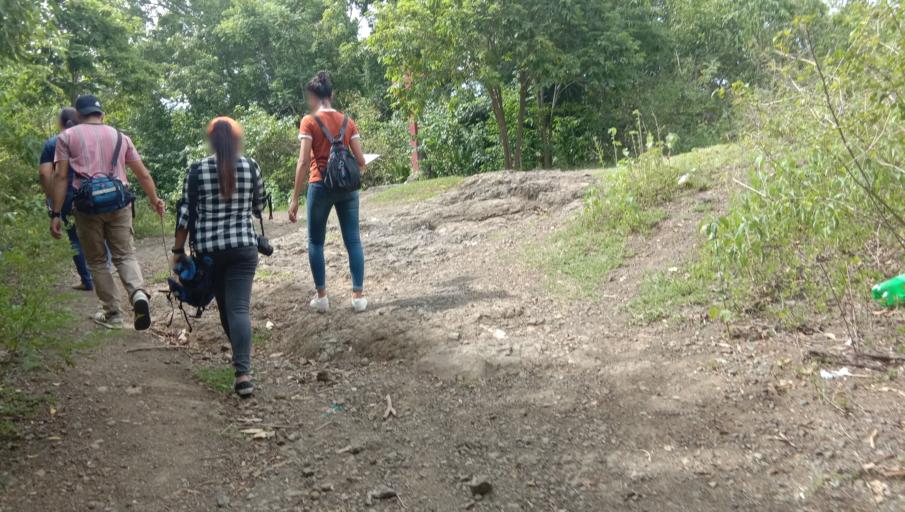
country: PH
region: Western Visayas
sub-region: Province of Capiz
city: Roxas City
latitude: 11.6079
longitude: 122.7066
